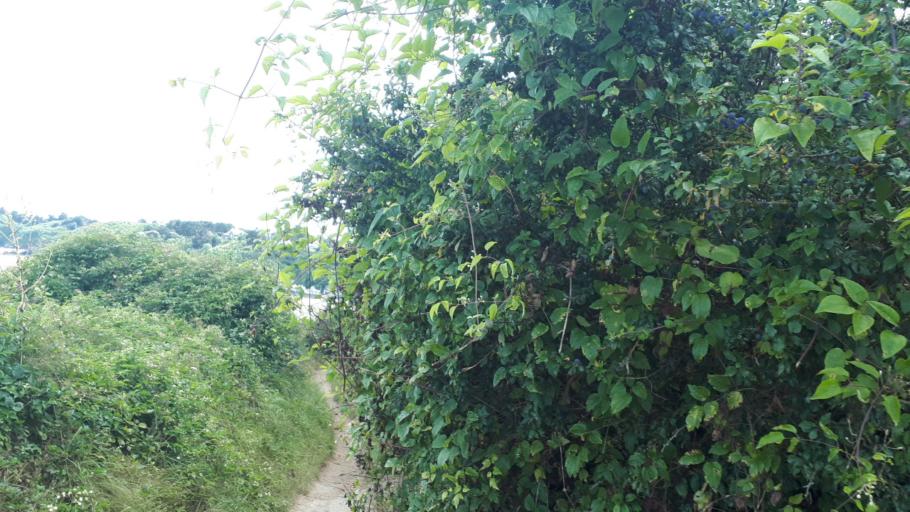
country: FR
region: Brittany
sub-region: Departement des Cotes-d'Armor
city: Etables-sur-Mer
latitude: 48.6288
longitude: -2.8203
